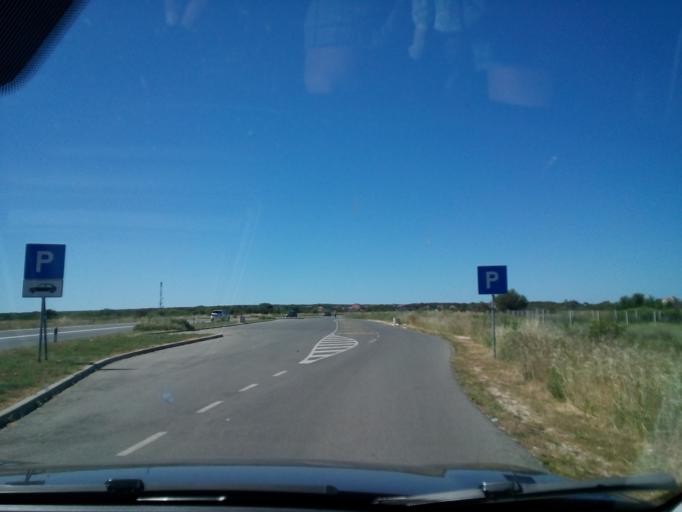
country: HR
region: Zadarska
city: Nin
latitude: 44.2309
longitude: 15.1806
